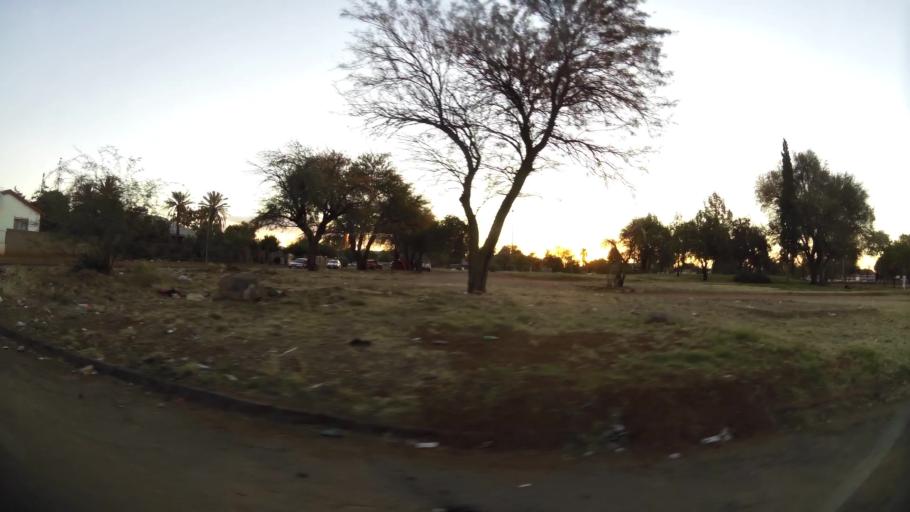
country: ZA
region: Northern Cape
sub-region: Frances Baard District Municipality
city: Kimberley
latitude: -28.7313
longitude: 24.7736
